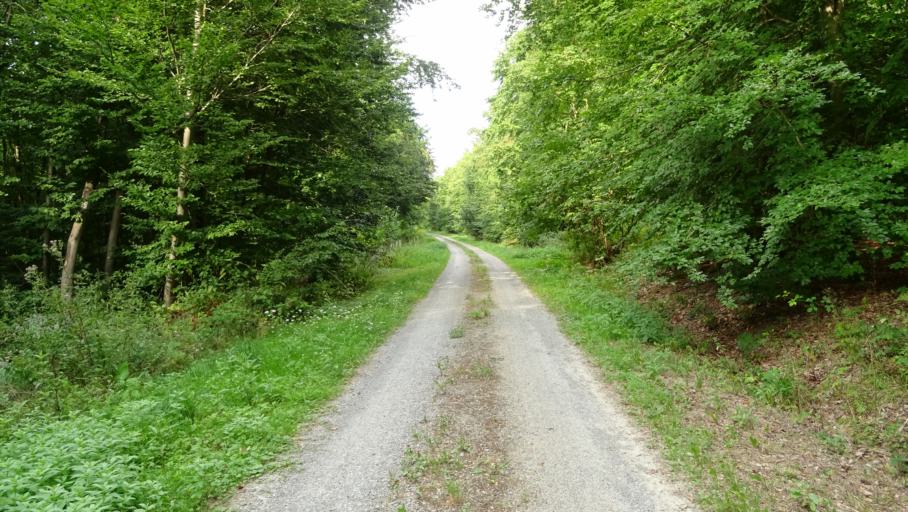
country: DE
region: Baden-Wuerttemberg
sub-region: Karlsruhe Region
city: Fahrenbach
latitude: 49.4146
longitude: 9.1099
